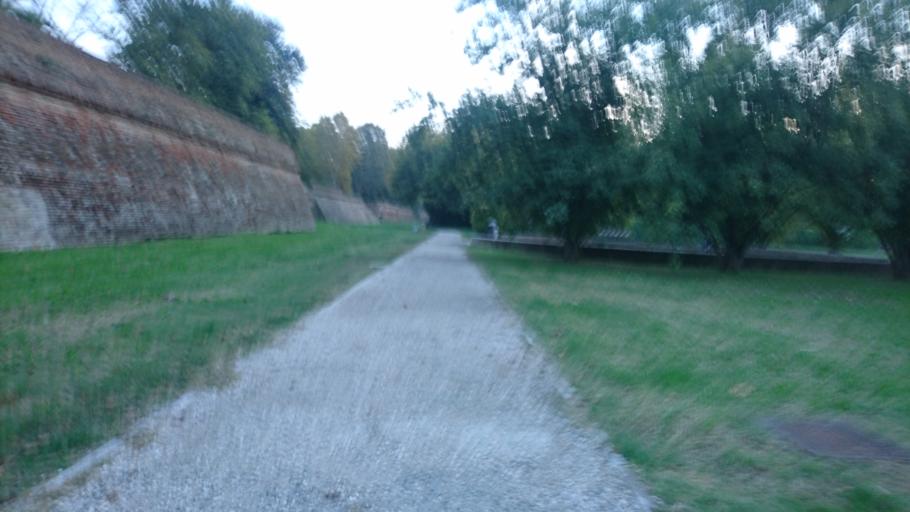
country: IT
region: Emilia-Romagna
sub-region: Provincia di Ferrara
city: Ferrara
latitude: 44.8478
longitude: 11.6133
